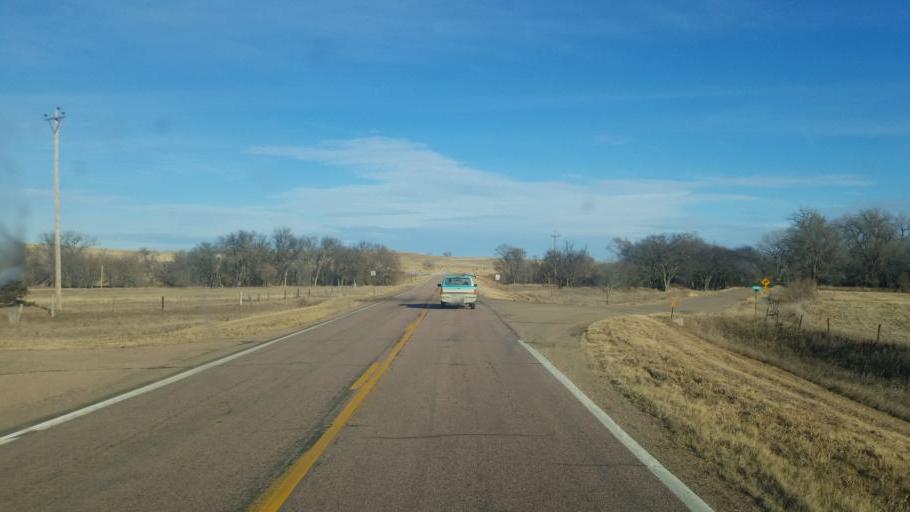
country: US
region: South Dakota
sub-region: Charles Mix County
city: Wagner
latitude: 42.8281
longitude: -98.4549
